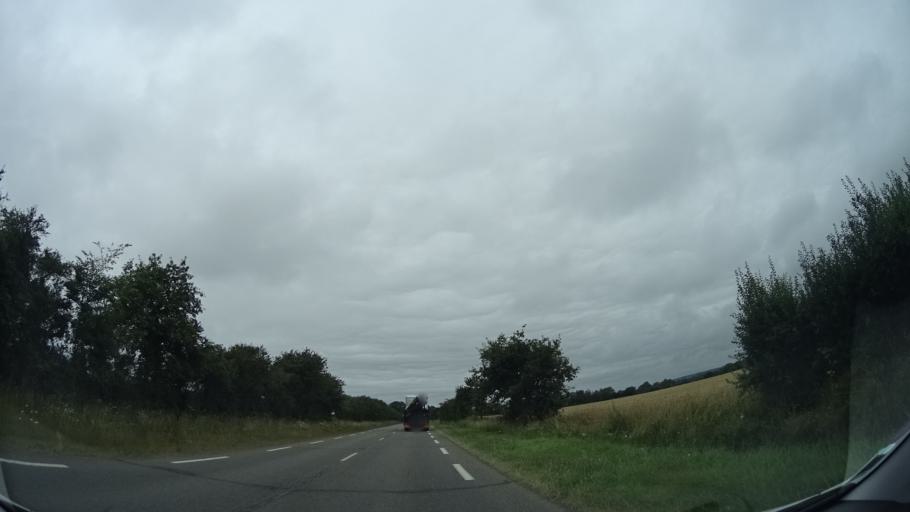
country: FR
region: Lower Normandy
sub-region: Departement de la Manche
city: Portbail
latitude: 49.3629
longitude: -1.7038
